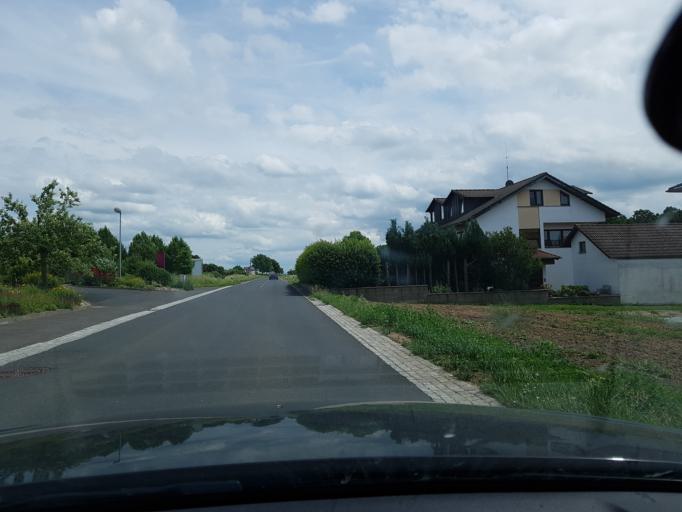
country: DE
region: Bavaria
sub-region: Regierungsbezirk Unterfranken
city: Nordheim
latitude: 49.8765
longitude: 10.1709
